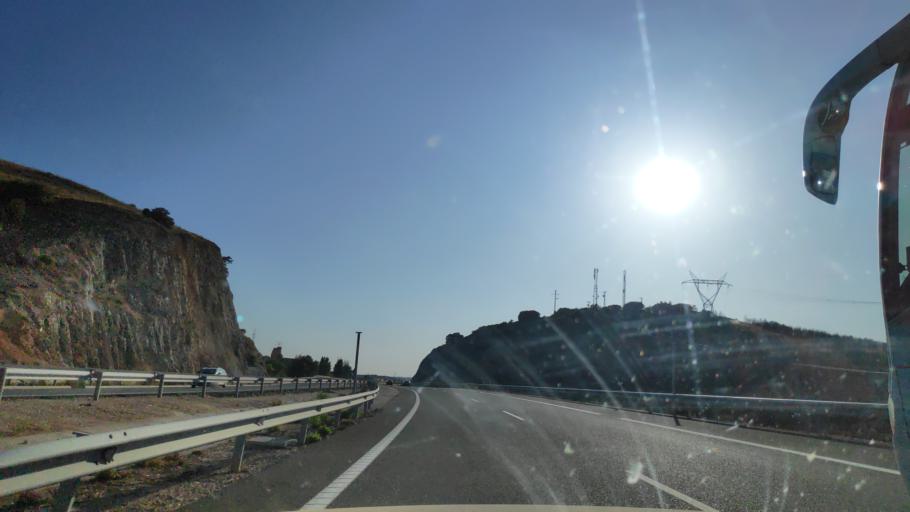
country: ES
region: Castille-La Mancha
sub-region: Provincia de Cuenca
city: Villares del Saz
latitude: 39.8602
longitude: -2.5352
